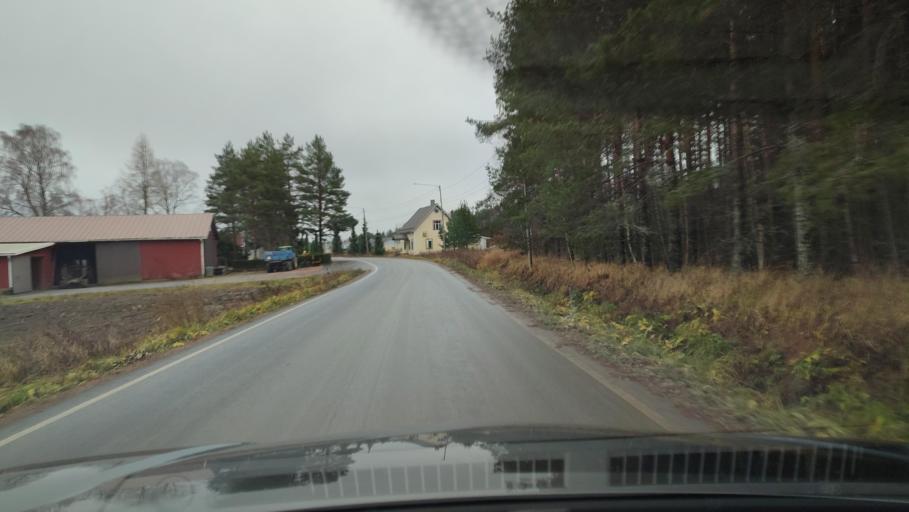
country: FI
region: Southern Ostrobothnia
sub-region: Suupohja
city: Karijoki
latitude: 62.1350
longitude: 21.6728
